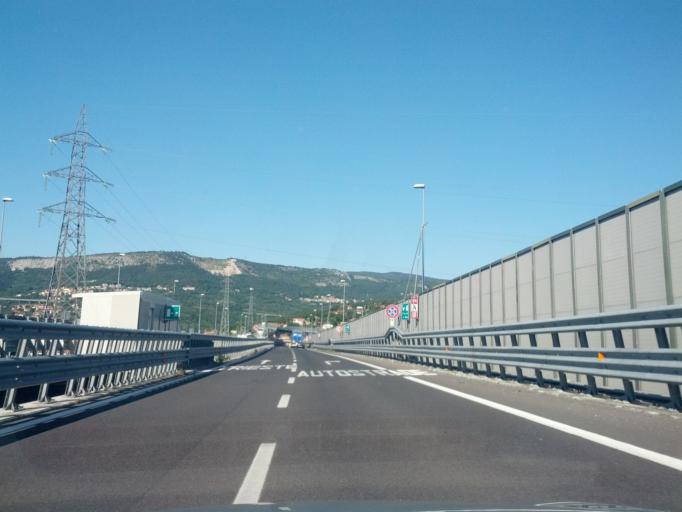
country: IT
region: Friuli Venezia Giulia
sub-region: Provincia di Trieste
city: Domio
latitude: 45.6051
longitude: 13.8260
